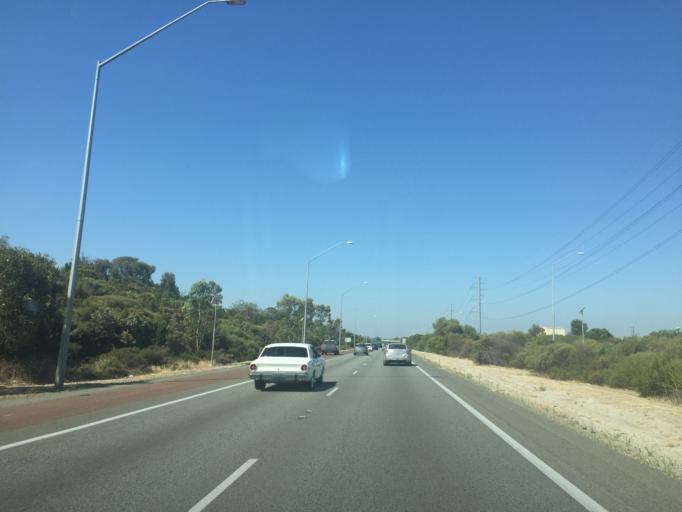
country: AU
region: Western Australia
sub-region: Canning
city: Willetton
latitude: -32.0630
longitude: 115.8972
